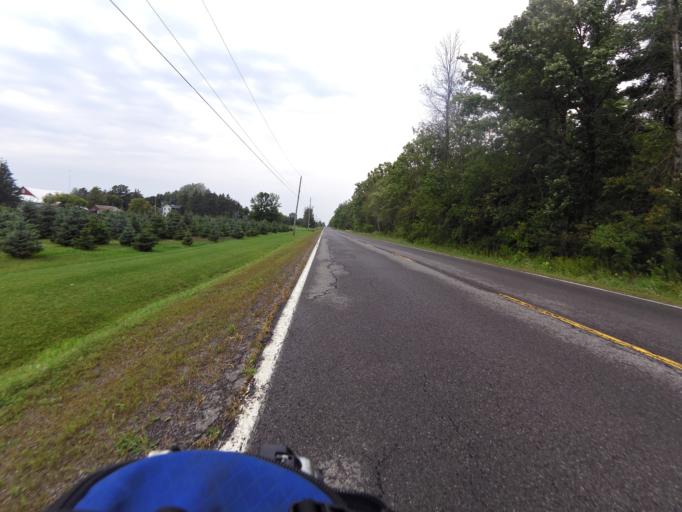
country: CA
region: Ontario
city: Ottawa
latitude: 45.1919
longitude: -75.4500
